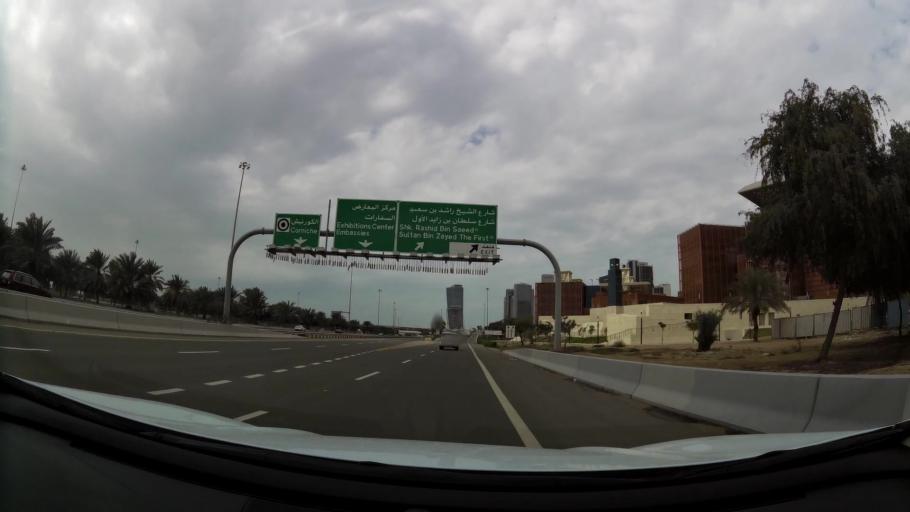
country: AE
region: Abu Dhabi
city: Abu Dhabi
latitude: 24.4144
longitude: 54.4478
